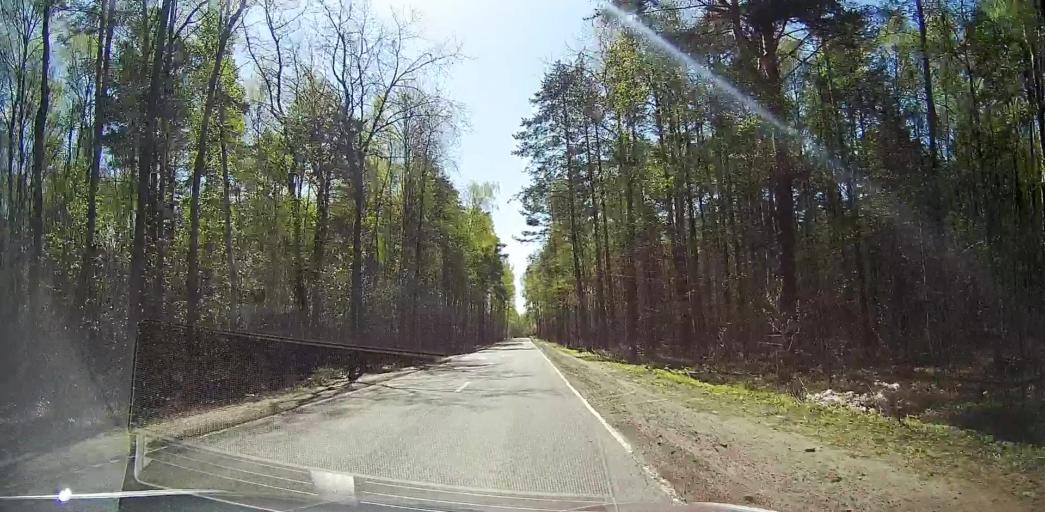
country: RU
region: Moskovskaya
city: Beloozerskiy
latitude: 55.4823
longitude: 38.4242
